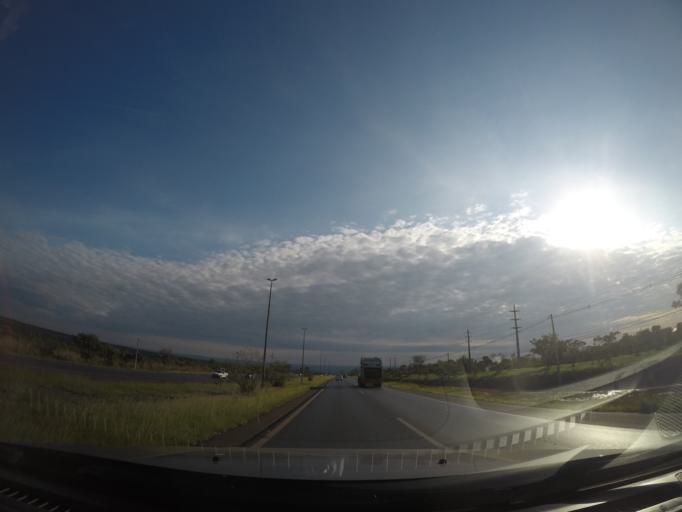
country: BR
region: Goias
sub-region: Planaltina
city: Planaltina
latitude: -15.6327
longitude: -47.7375
